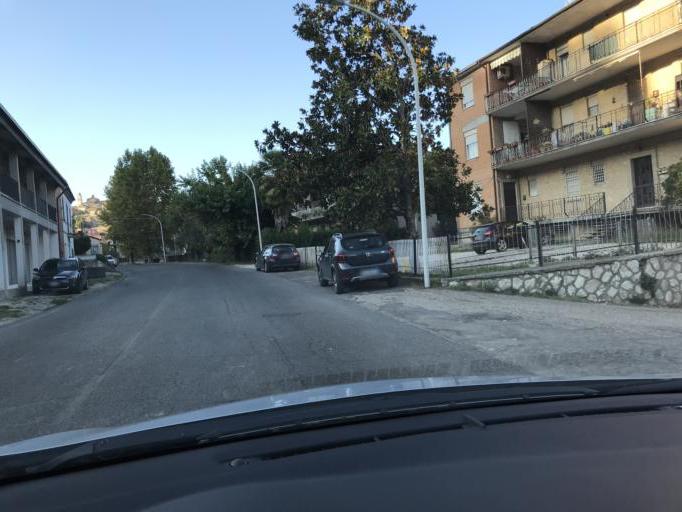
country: IT
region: Latium
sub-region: Provincia di Viterbo
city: Orte
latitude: 42.4527
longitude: 12.3882
